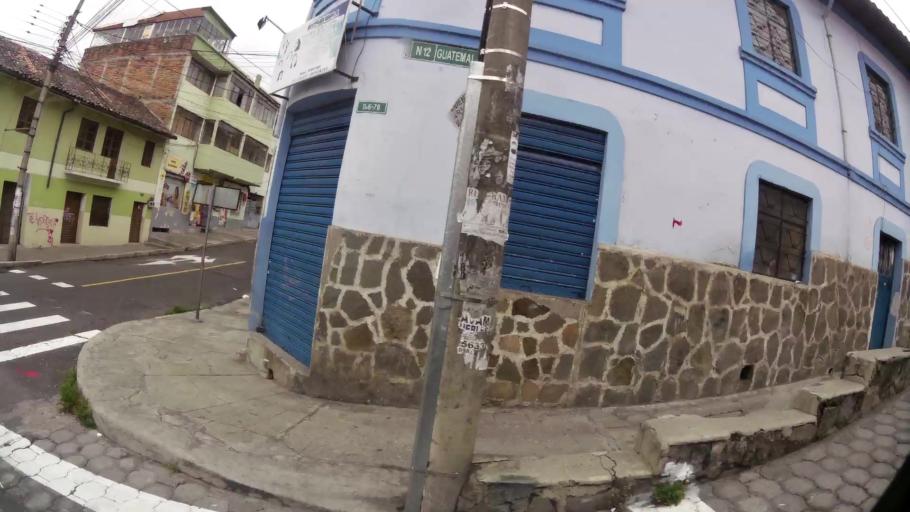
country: EC
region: Pichincha
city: Quito
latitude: -0.2124
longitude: -78.5089
